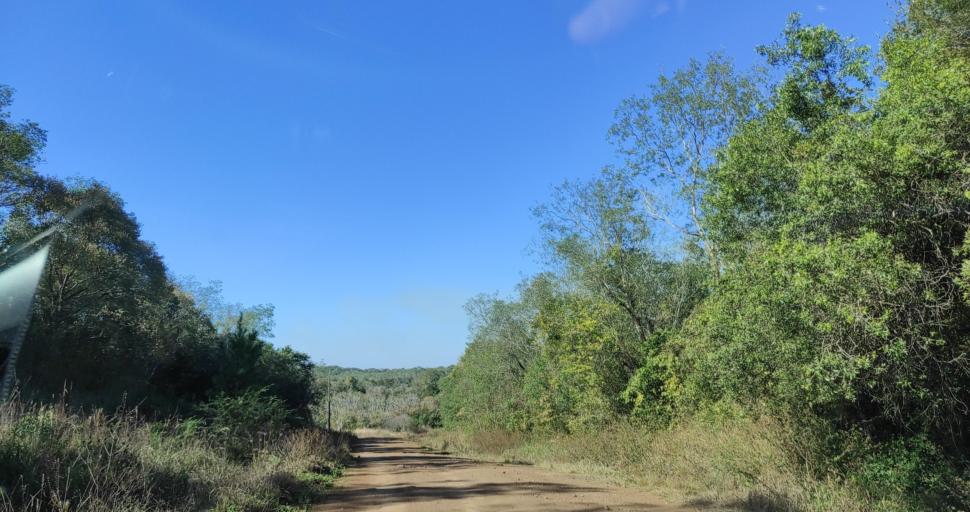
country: AR
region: Misiones
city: Cerro Cora
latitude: -27.6313
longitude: -55.6939
